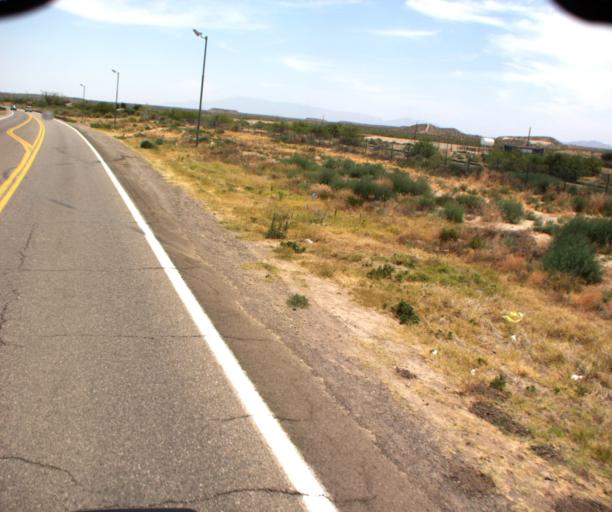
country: US
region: Arizona
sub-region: Graham County
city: Bylas
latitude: 33.1191
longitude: -110.1097
